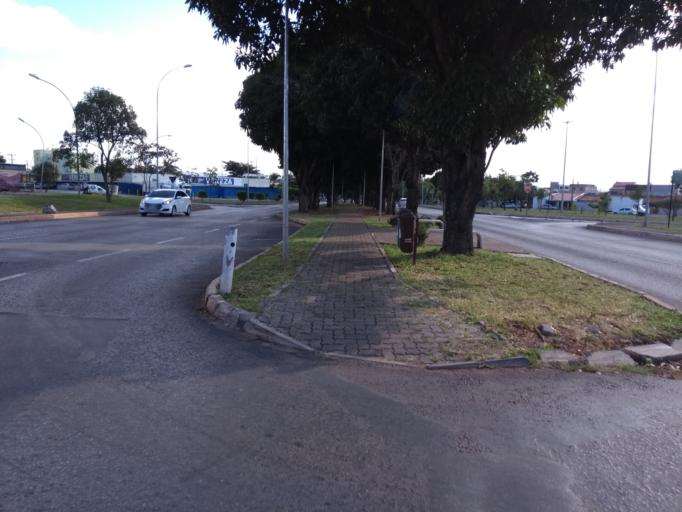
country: BR
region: Federal District
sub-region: Brasilia
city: Brasilia
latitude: -15.7905
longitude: -47.9360
